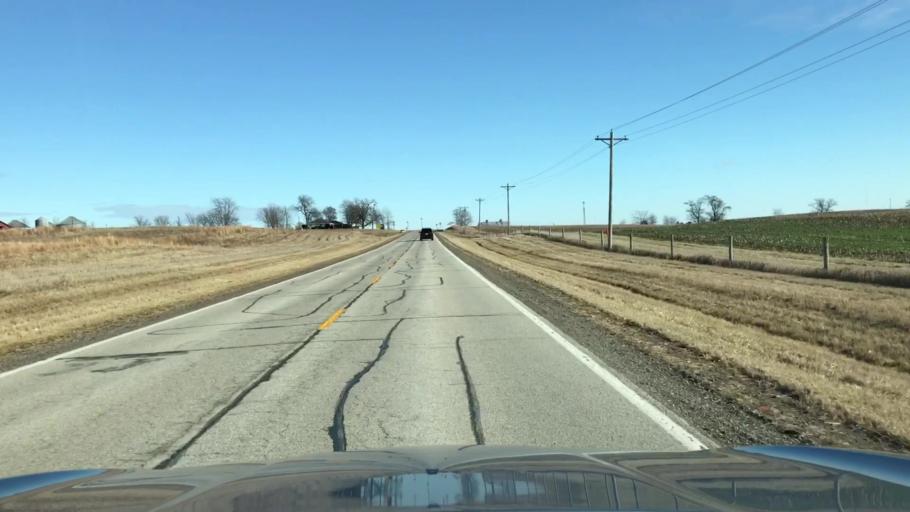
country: US
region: Illinois
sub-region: McLean County
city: Lexington
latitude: 40.6452
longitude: -88.8224
